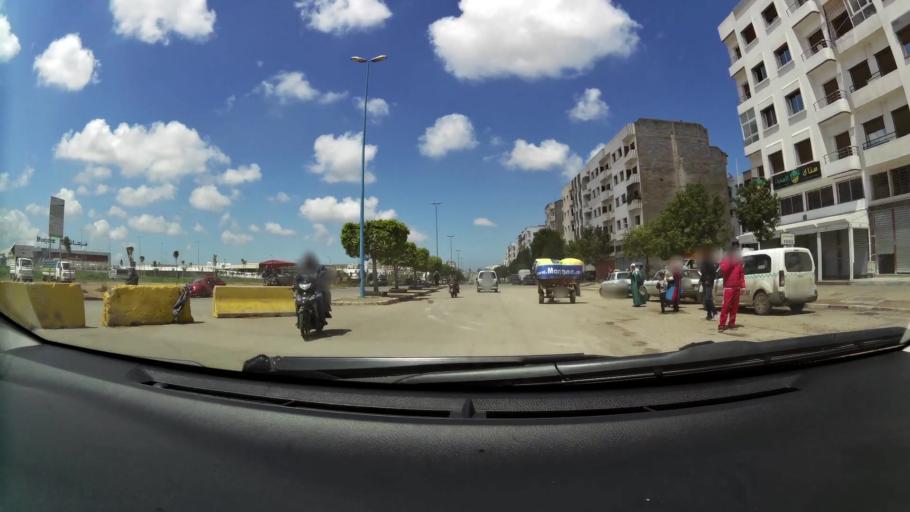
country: MA
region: Grand Casablanca
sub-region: Mediouna
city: Tit Mellil
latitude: 33.5468
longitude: -7.5458
